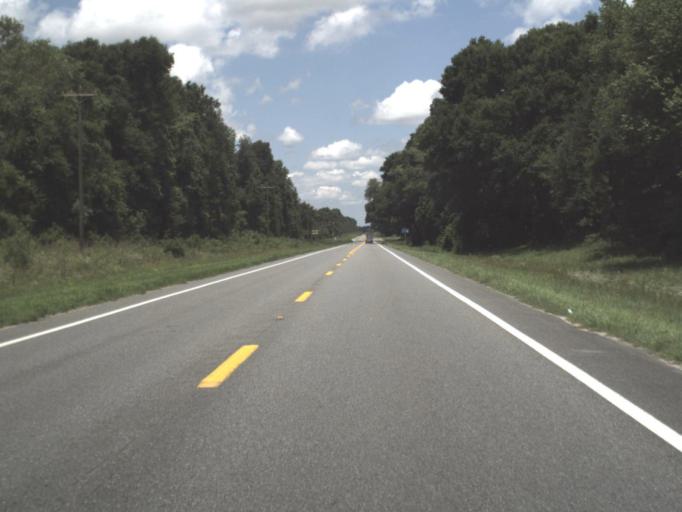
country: US
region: Florida
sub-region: Alachua County
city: High Springs
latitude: 29.8816
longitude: -82.6646
